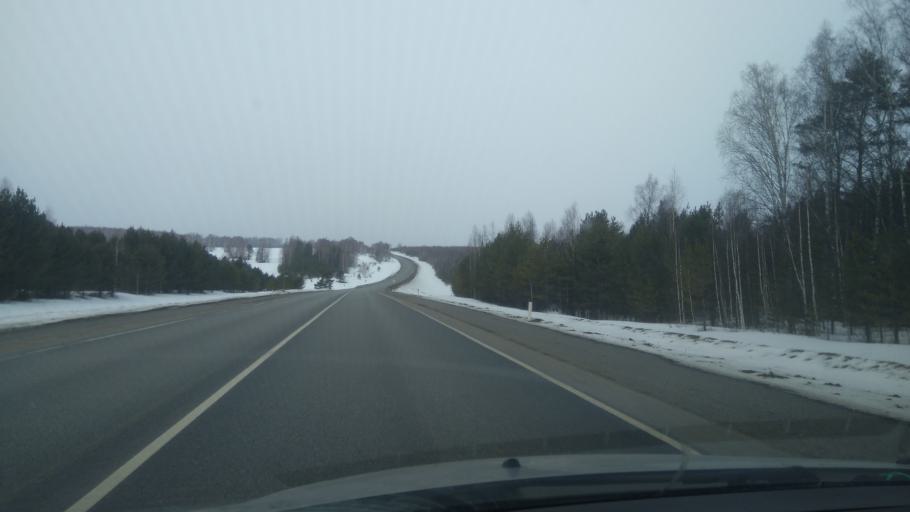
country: RU
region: Perm
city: Suksun
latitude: 56.9241
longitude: 57.5630
